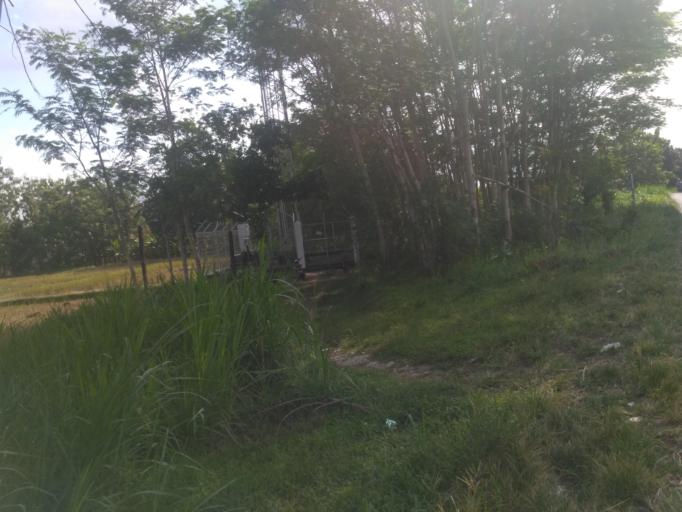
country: ID
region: Daerah Istimewa Yogyakarta
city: Godean
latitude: -7.7453
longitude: 110.3193
